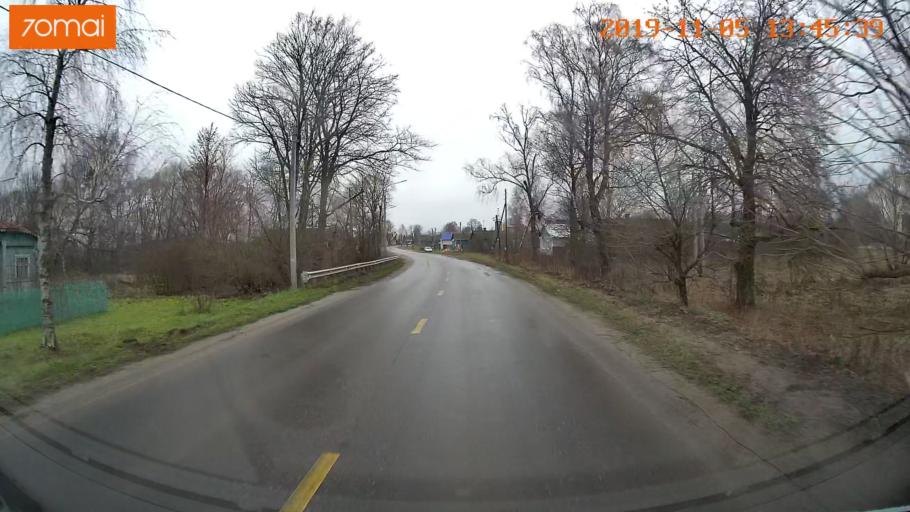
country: RU
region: Ivanovo
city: Shuya
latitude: 56.9904
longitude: 41.4121
